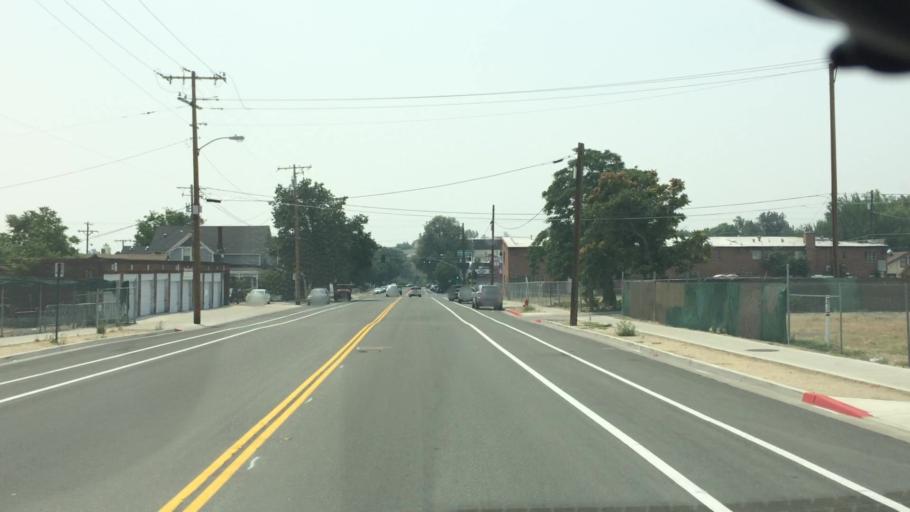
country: US
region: Nevada
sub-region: Washoe County
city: Reno
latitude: 39.5270
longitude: -119.8203
